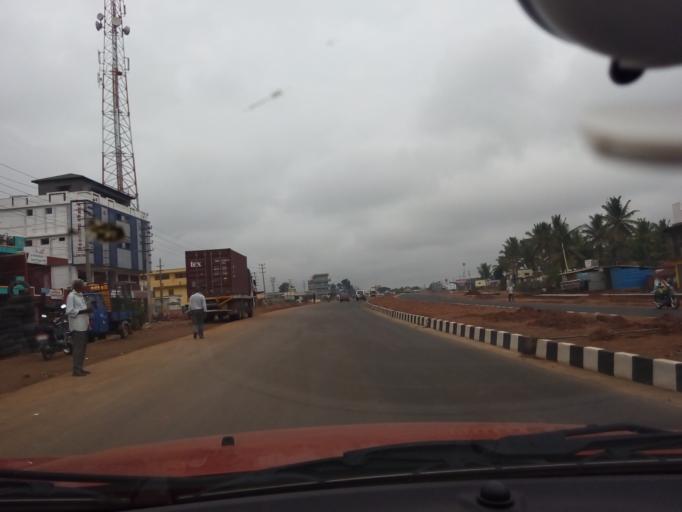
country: IN
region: Karnataka
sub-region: Hassan
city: Shravanabelagola
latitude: 12.9519
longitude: 76.5732
